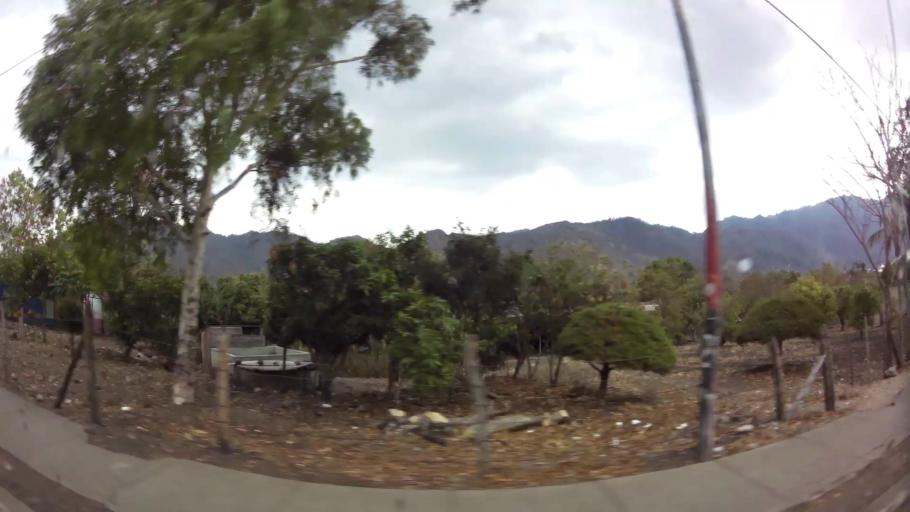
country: NI
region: Jinotega
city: Jinotega
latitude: 13.0954
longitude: -86.0069
